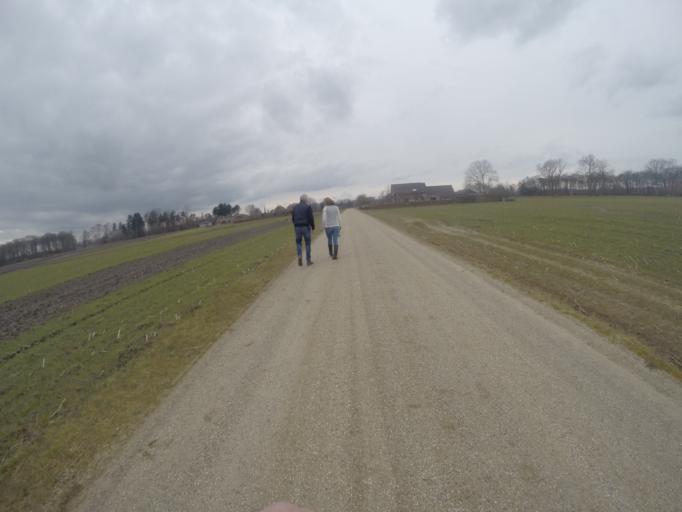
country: NL
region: Gelderland
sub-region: Gemeente Bronckhorst
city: Hengelo
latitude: 52.0491
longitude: 6.3399
